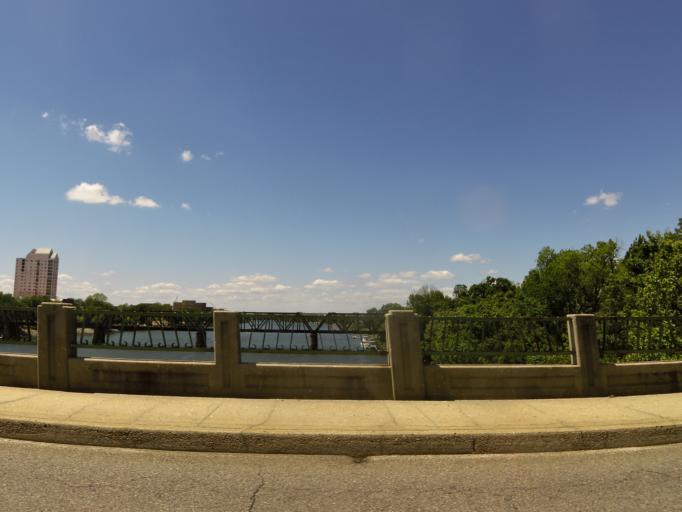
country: US
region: Georgia
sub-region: Richmond County
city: Augusta
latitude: 33.4773
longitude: -81.9567
